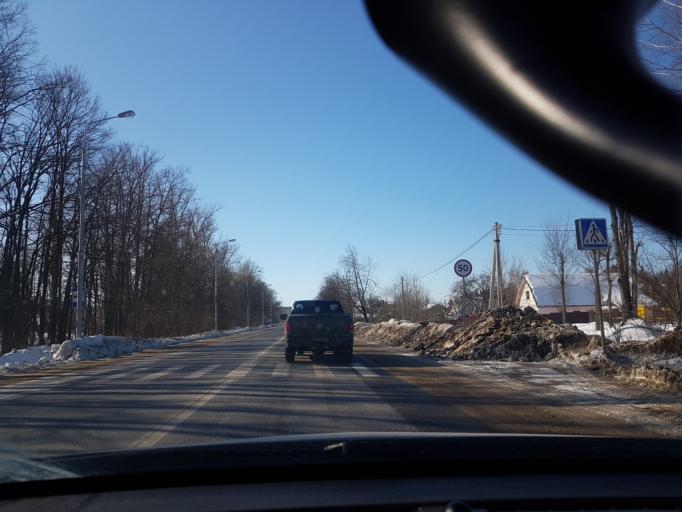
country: RU
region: Moskovskaya
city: Kostrovo
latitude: 55.9157
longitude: 36.6915
